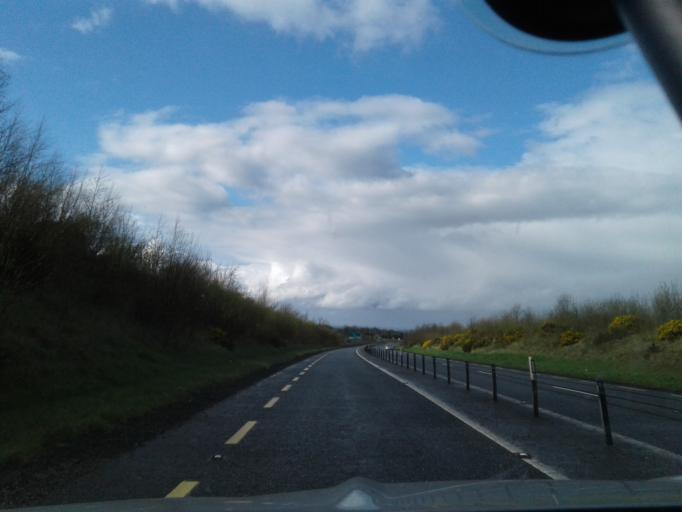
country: IE
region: Ulster
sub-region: County Monaghan
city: Castleblayney
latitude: 54.1976
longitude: -6.8377
